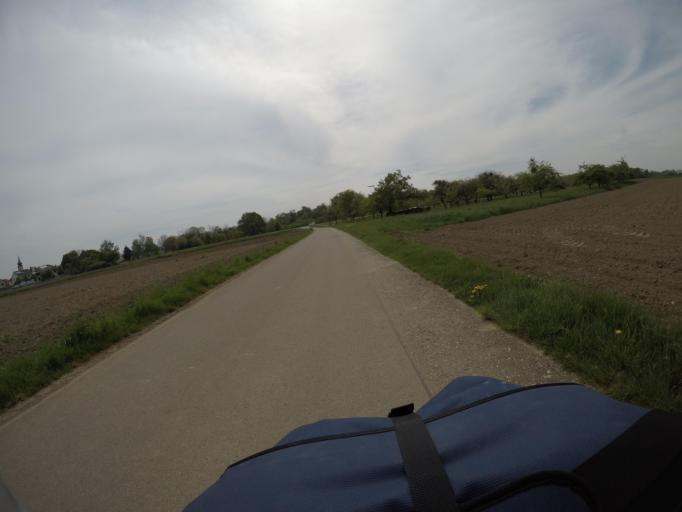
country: DE
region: Baden-Wuerttemberg
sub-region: Karlsruhe Region
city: Schwarzach
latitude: 48.7627
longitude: 8.0447
